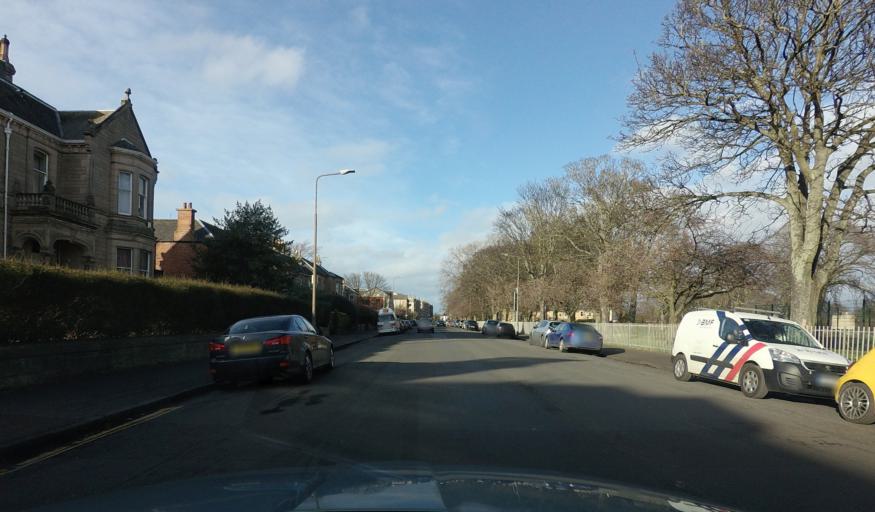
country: GB
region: Scotland
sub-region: Edinburgh
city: Edinburgh
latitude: 55.9740
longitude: -3.1957
